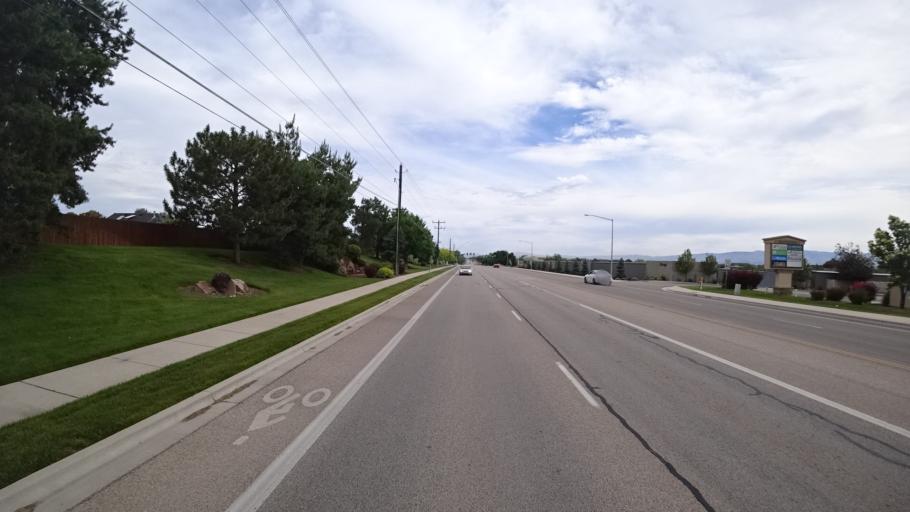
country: US
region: Idaho
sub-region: Ada County
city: Meridian
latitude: 43.5806
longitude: -116.3546
